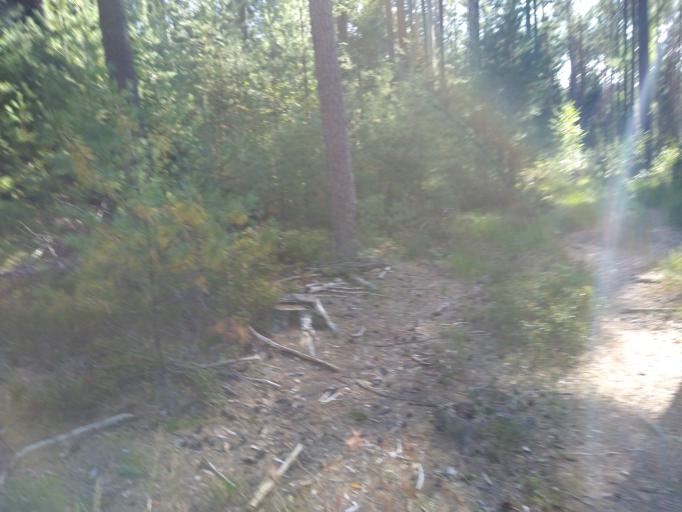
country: DE
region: Bavaria
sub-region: Regierungsbezirk Mittelfranken
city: Seukendorf
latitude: 49.4653
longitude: 10.9170
